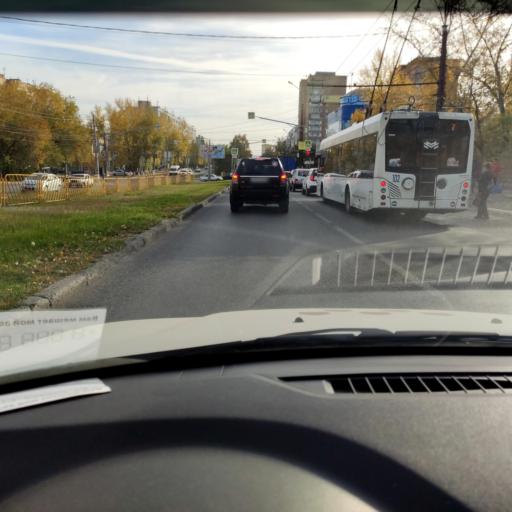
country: RU
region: Samara
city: Zhigulevsk
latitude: 53.4825
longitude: 49.4739
